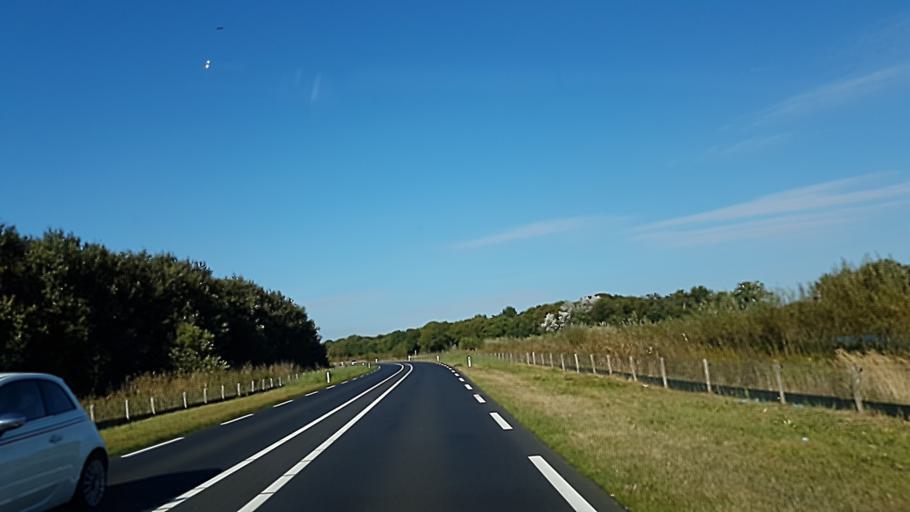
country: NL
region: North Brabant
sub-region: Gemeente Woensdrecht
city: Woensdrecht
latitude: 51.4322
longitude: 4.3403
